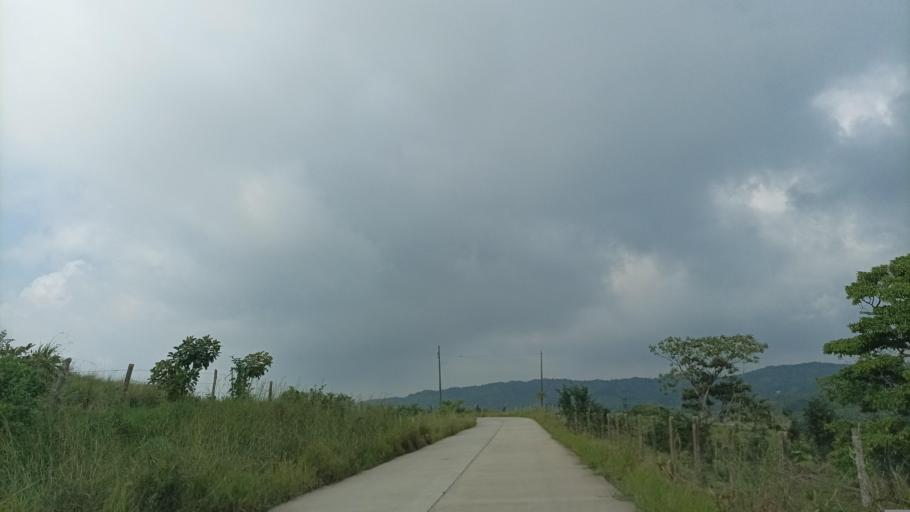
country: MX
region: Veracruz
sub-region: Moloacan
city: Tlacuilolapan
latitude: 18.0873
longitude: -94.2870
